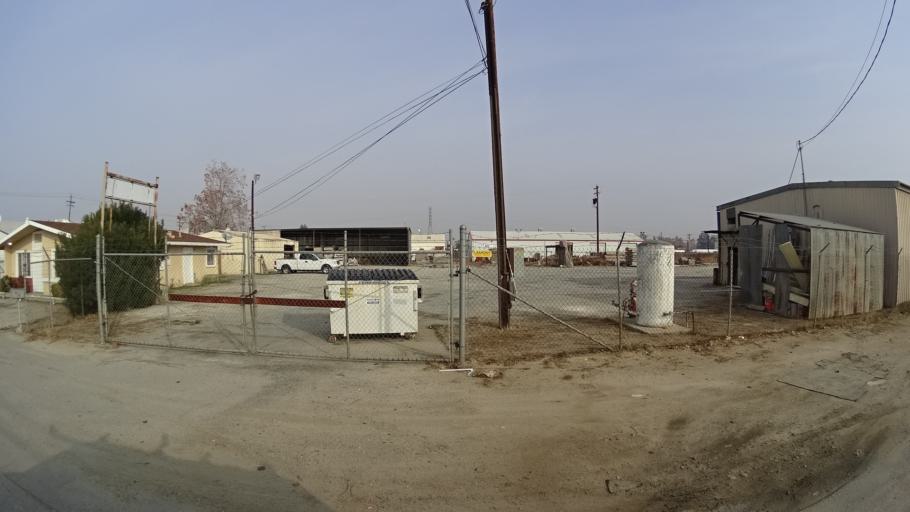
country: US
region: California
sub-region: Kern County
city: Bakersfield
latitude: 35.3940
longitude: -119.0421
